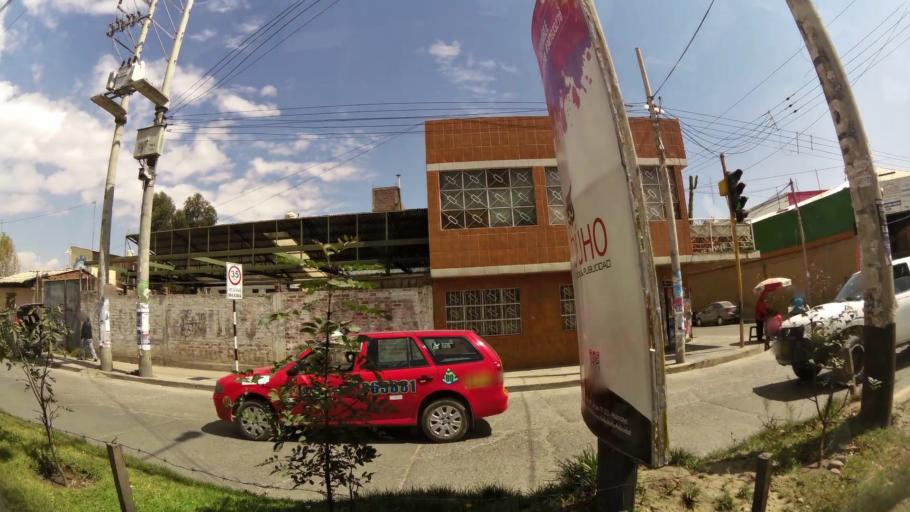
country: PE
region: Junin
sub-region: Provincia de Huancayo
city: El Tambo
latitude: -12.0667
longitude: -75.2169
